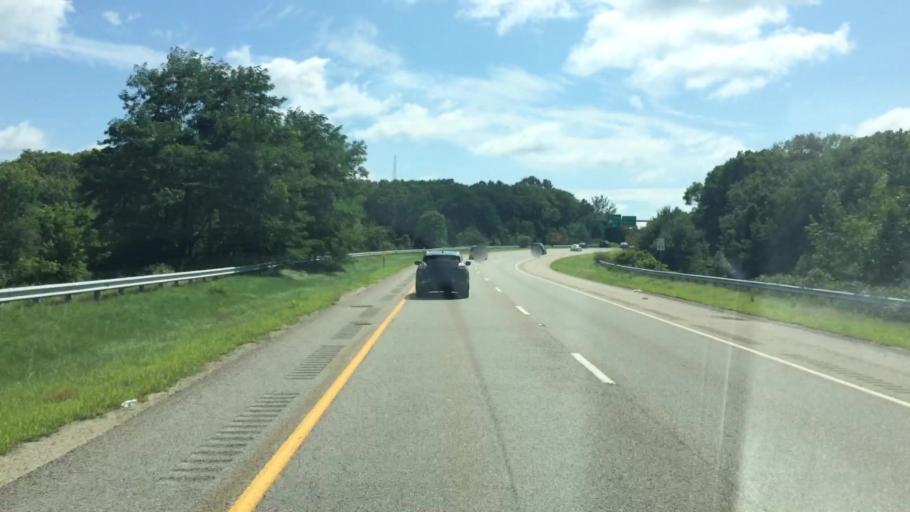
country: US
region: Rhode Island
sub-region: Providence County
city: Cumberland Hill
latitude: 41.9544
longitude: -71.4834
